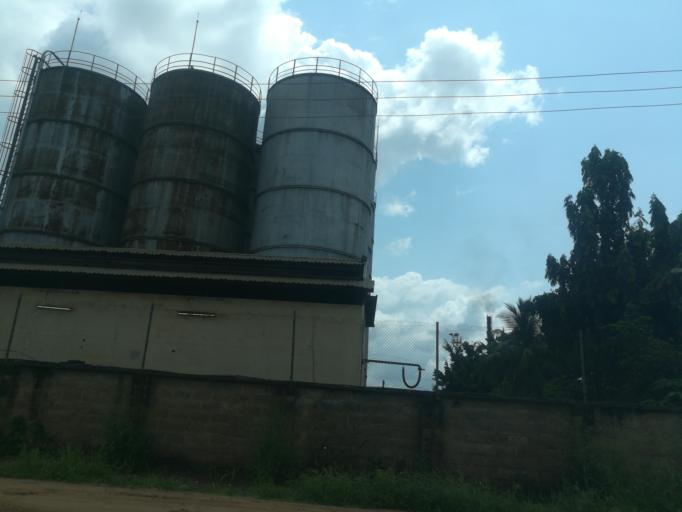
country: NG
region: Oyo
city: Ibadan
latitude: 7.3588
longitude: 3.8475
